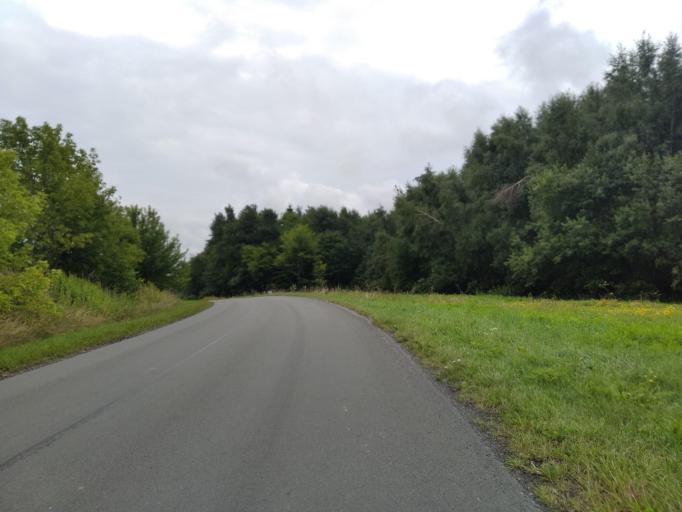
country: PL
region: Subcarpathian Voivodeship
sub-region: Powiat przemyski
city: Dubiecko
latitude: 49.7142
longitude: 22.3261
